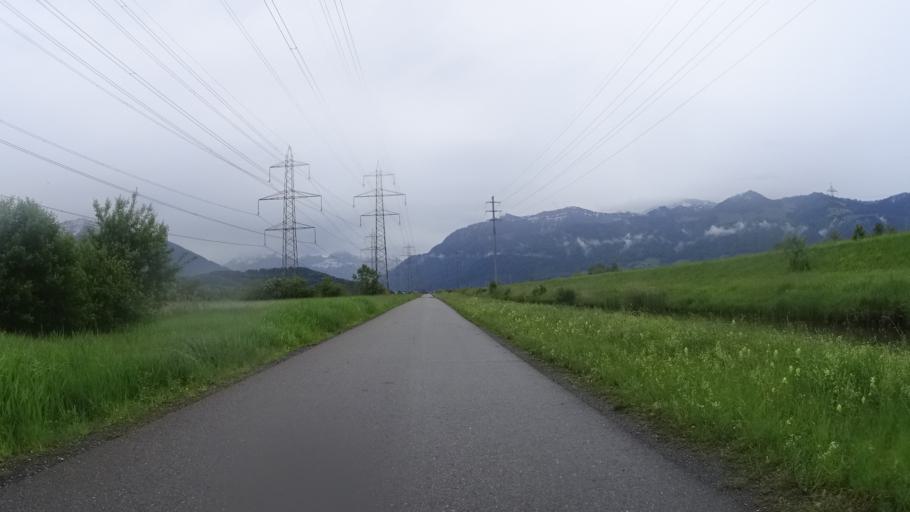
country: CH
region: Saint Gallen
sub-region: Wahlkreis See-Gaster
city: Uznach
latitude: 47.2101
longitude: 8.9776
